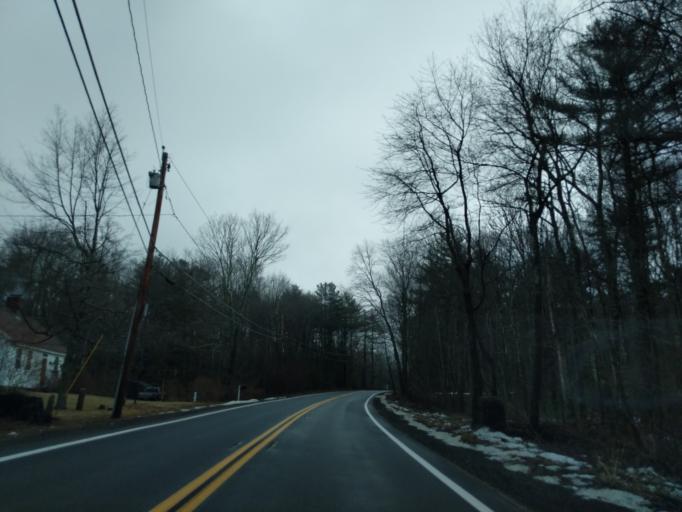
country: US
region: Massachusetts
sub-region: Worcester County
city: Douglas
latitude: 42.0555
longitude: -71.7611
